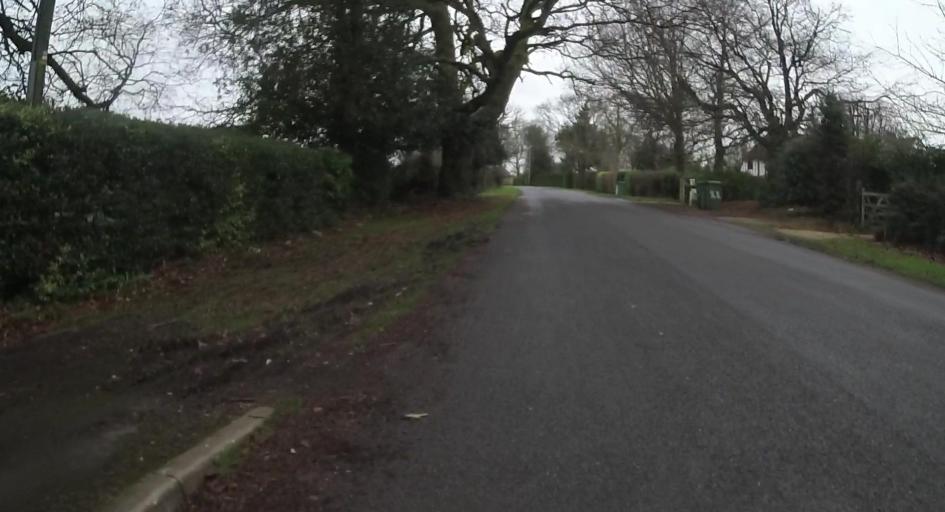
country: GB
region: England
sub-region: Hampshire
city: Four Marks
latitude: 51.1075
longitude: -1.0291
